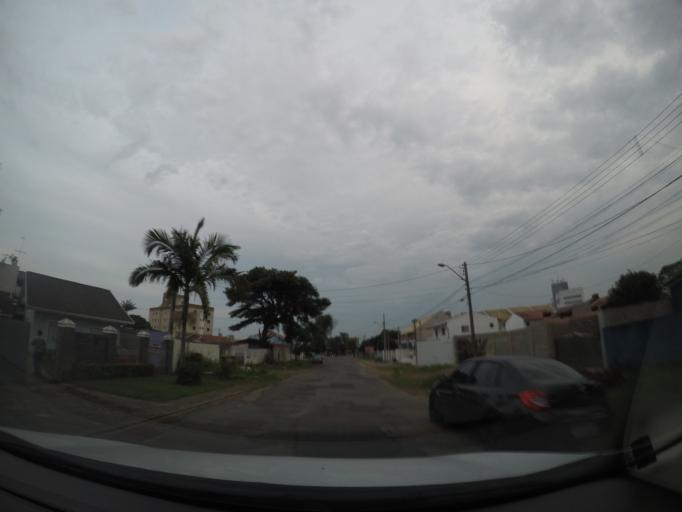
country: BR
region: Parana
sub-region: Sao Jose Dos Pinhais
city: Sao Jose dos Pinhais
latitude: -25.5154
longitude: -49.2328
